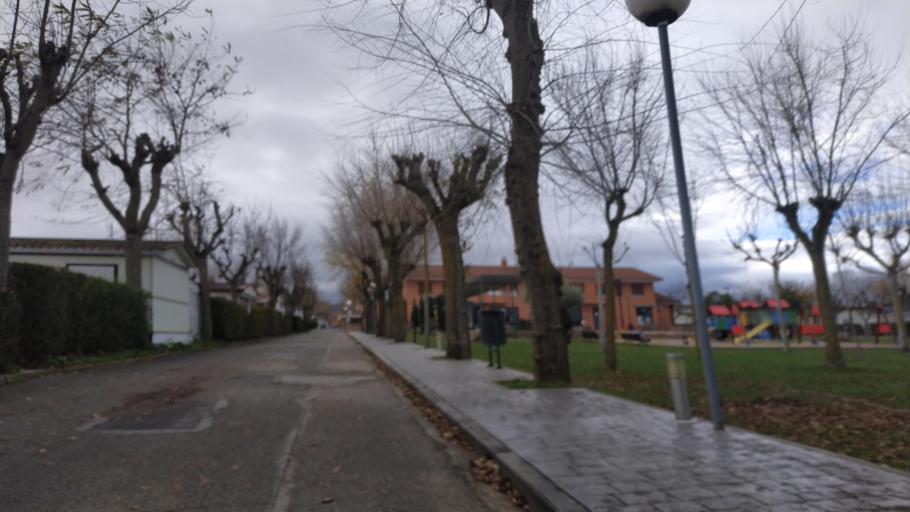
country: ES
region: La Rioja
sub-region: Provincia de La Rioja
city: Banares
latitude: 42.4434
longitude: -2.9153
